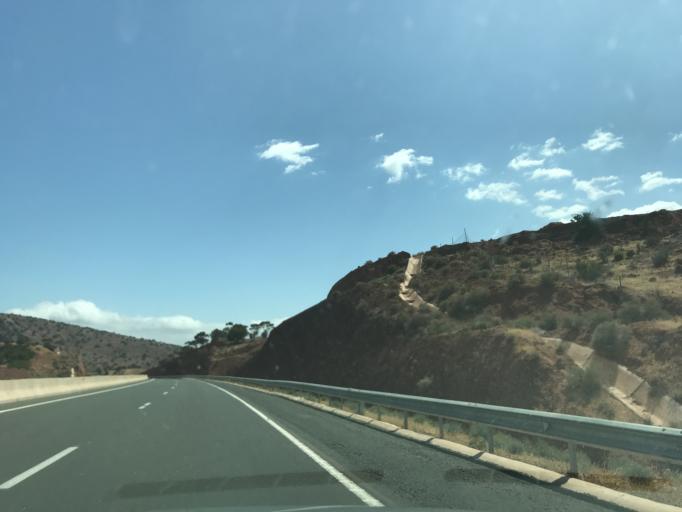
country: MA
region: Souss-Massa-Draa
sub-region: Taroudannt
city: Bigoudine
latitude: 30.7413
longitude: -9.1837
